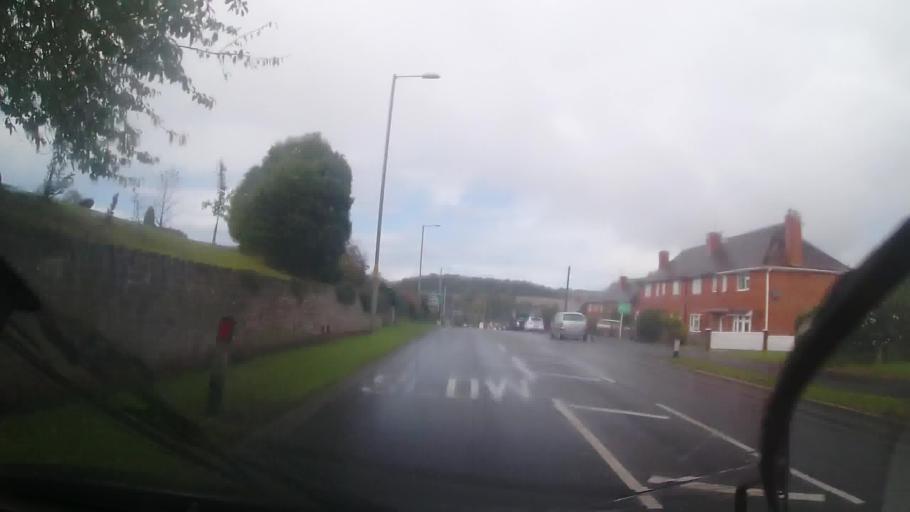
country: GB
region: England
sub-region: Shropshire
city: Much Wenlock
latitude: 52.5924
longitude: -2.5575
